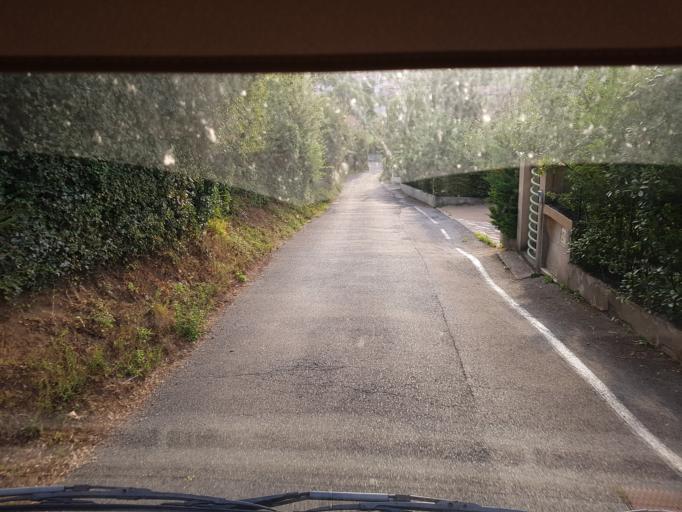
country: FR
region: Rhone-Alpes
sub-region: Departement du Rhone
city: Dardilly
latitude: 45.8184
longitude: 4.7538
